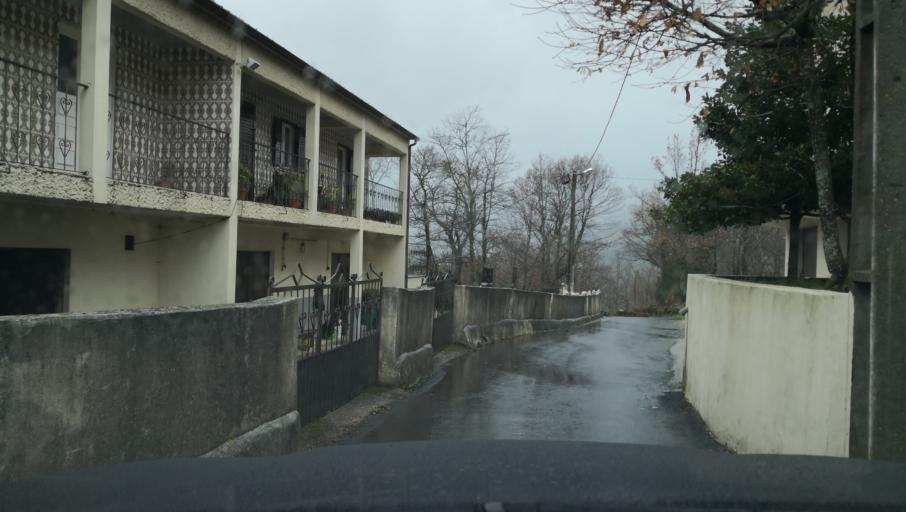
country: PT
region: Vila Real
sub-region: Santa Marta de Penaguiao
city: Santa Marta de Penaguiao
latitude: 41.2831
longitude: -7.8630
